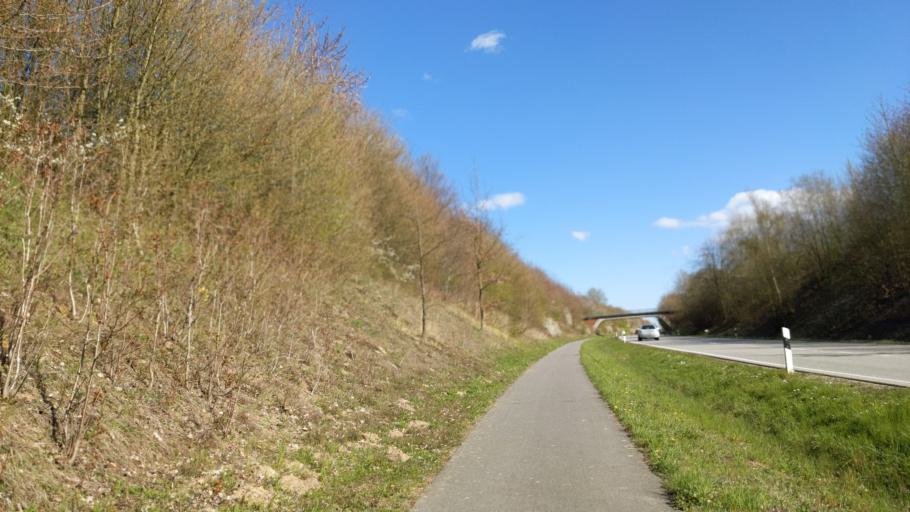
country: DE
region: Schleswig-Holstein
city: Eutin
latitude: 54.1226
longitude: 10.6012
